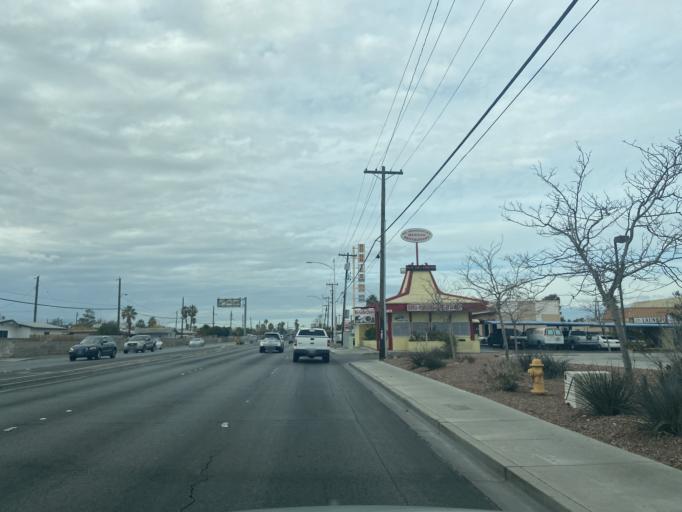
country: US
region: Nevada
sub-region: Clark County
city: Las Vegas
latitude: 36.1826
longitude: -115.1804
